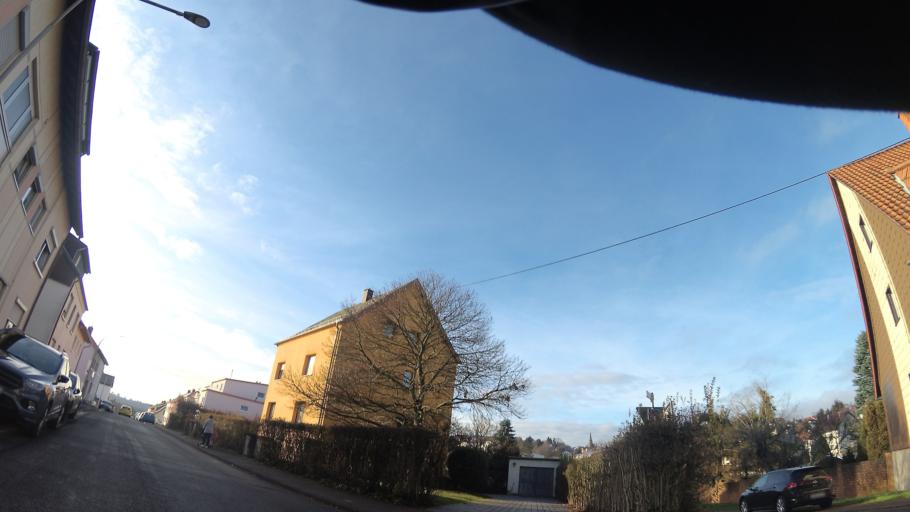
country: DE
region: Saarland
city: Spiesen-Elversberg
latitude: 49.3105
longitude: 7.1400
